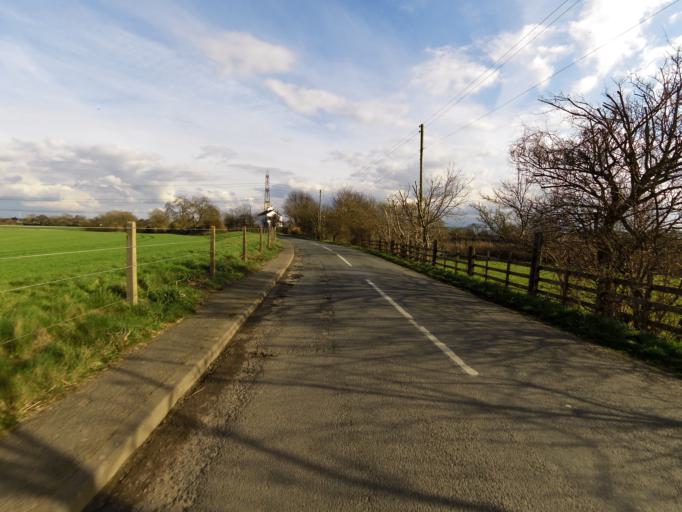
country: GB
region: England
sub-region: East Riding of Yorkshire
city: Snaith
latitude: 53.6917
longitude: -1.0492
